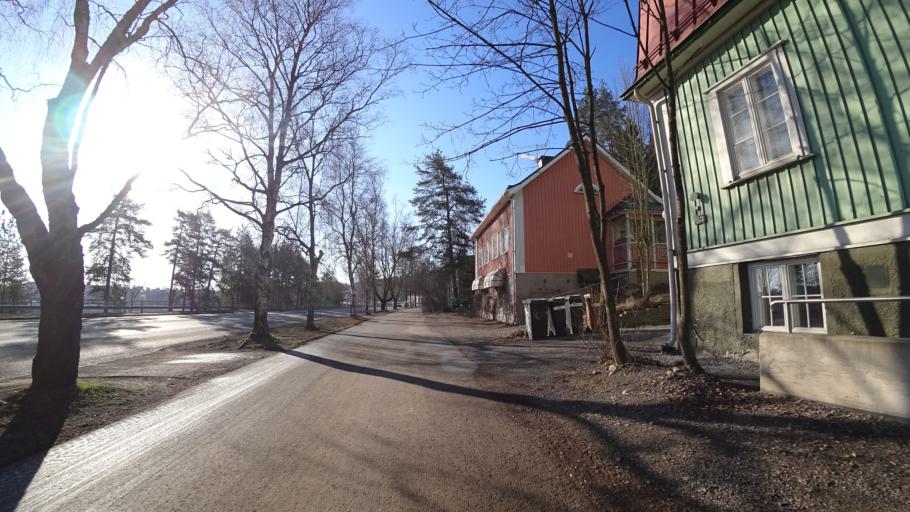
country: FI
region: Pirkanmaa
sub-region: Tampere
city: Tampere
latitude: 61.5007
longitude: 23.7234
